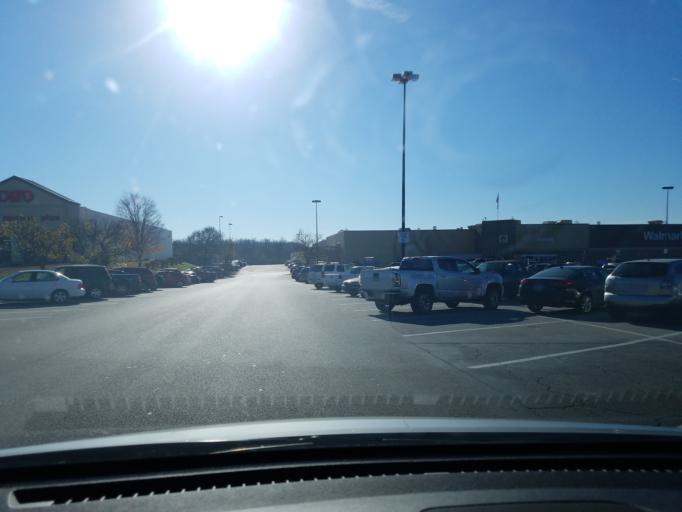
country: US
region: Arkansas
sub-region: Carroll County
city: Berryville
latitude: 36.3769
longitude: -93.5853
